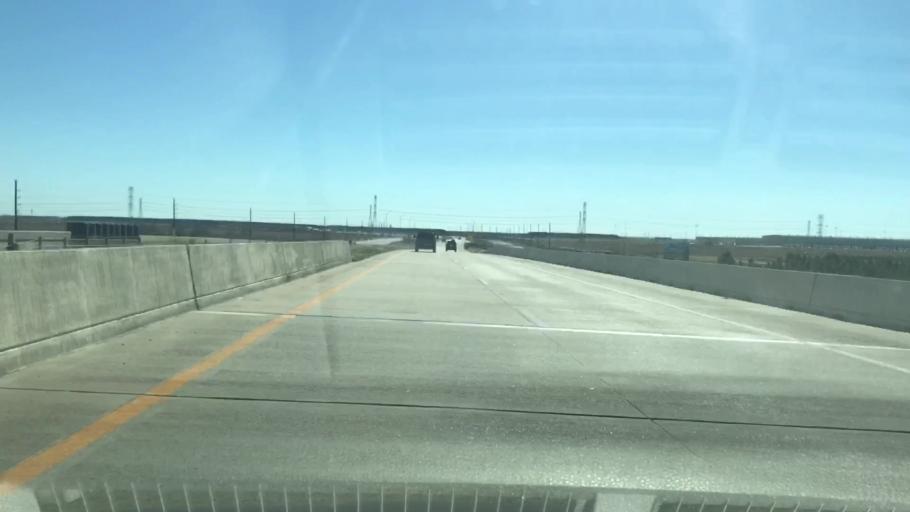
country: US
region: Texas
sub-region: Harris County
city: Cypress
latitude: 29.9216
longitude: -95.7622
